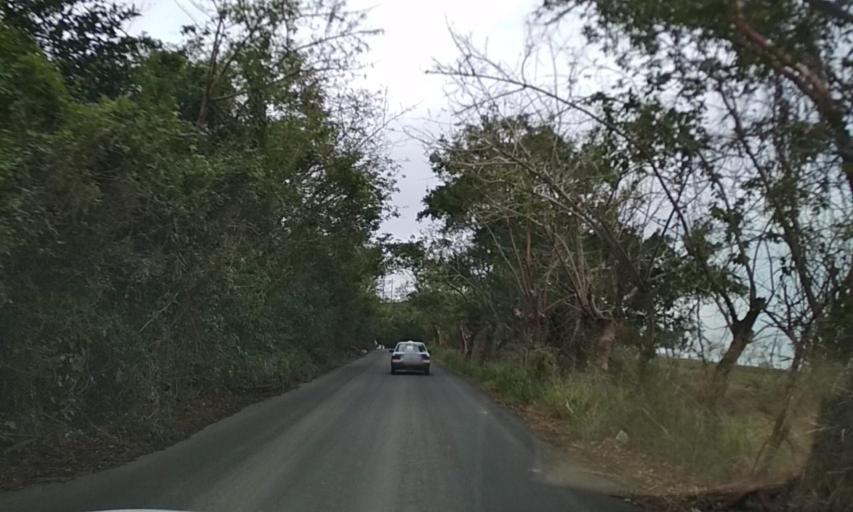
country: MX
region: Veracruz
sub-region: Coatzintla
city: Manuel Maria Contreras
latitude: 20.4441
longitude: -97.5043
